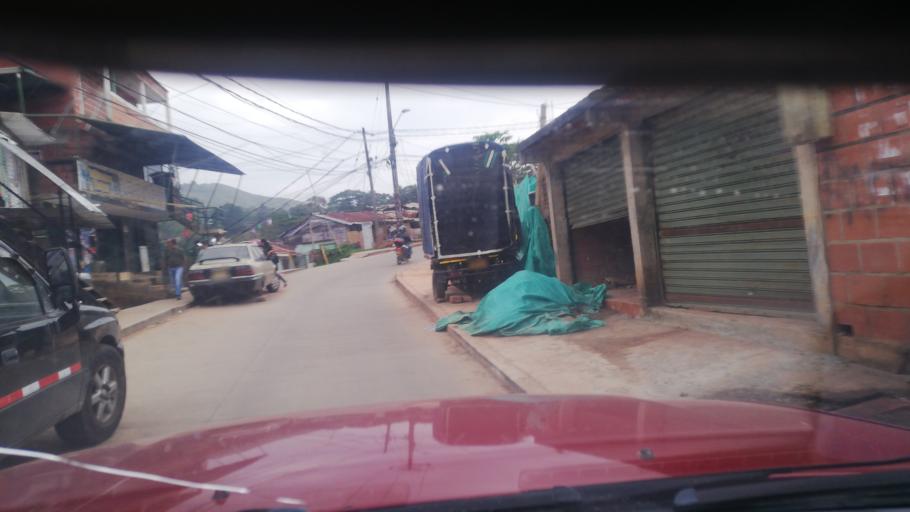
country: CO
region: Valle del Cauca
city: Cali
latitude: 3.4855
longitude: -76.5484
